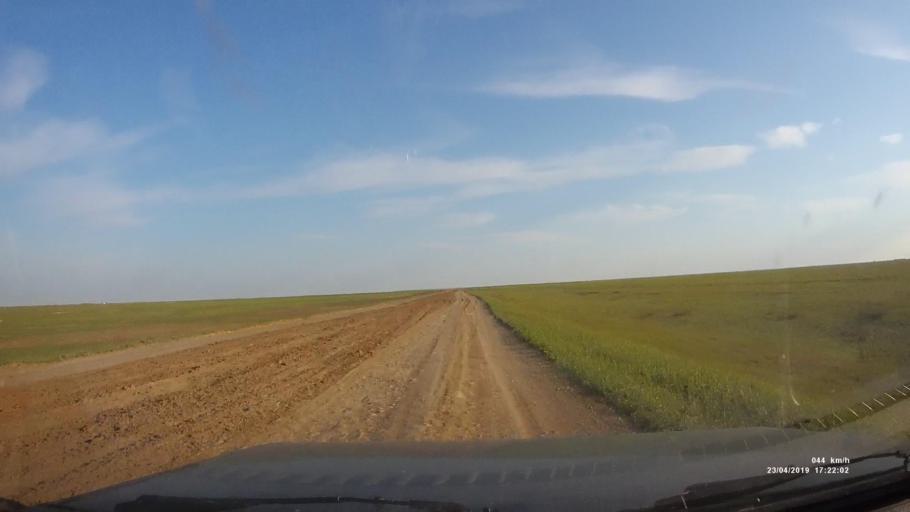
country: RU
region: Kalmykiya
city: Priyutnoye
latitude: 46.1716
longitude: 43.5061
